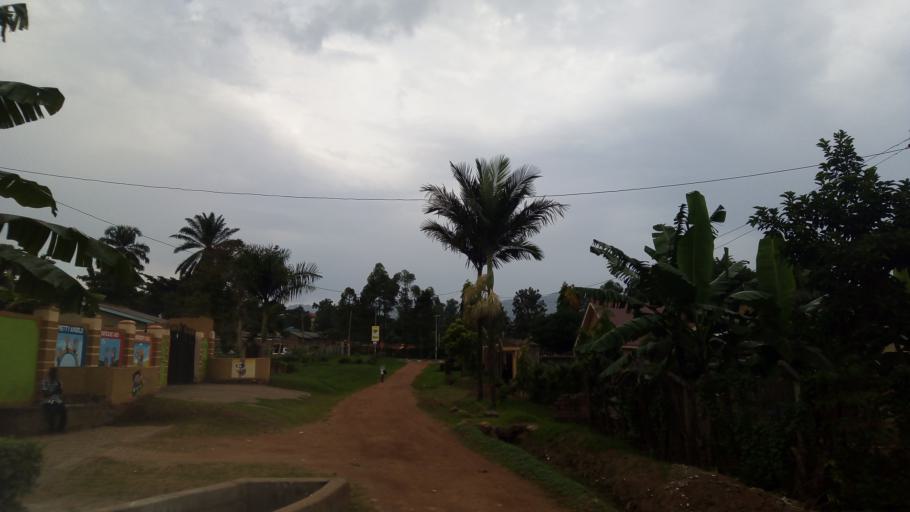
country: UG
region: Eastern Region
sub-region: Mbale District
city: Mbale
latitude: 1.0761
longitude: 34.1707
